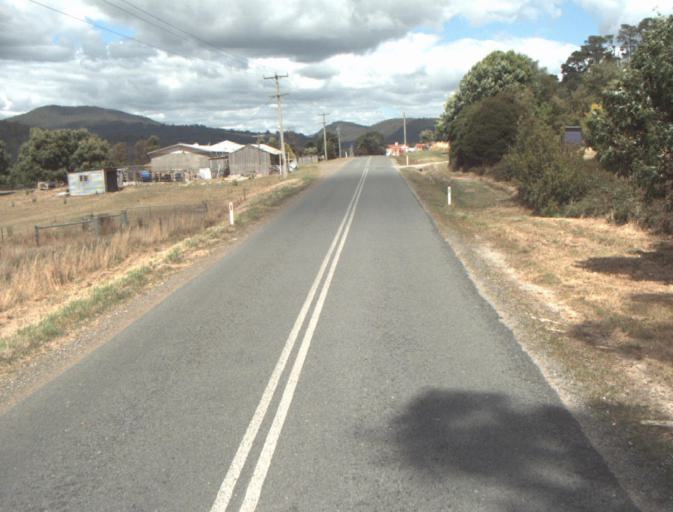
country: AU
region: Tasmania
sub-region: Launceston
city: Mayfield
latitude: -41.2376
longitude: 147.1339
